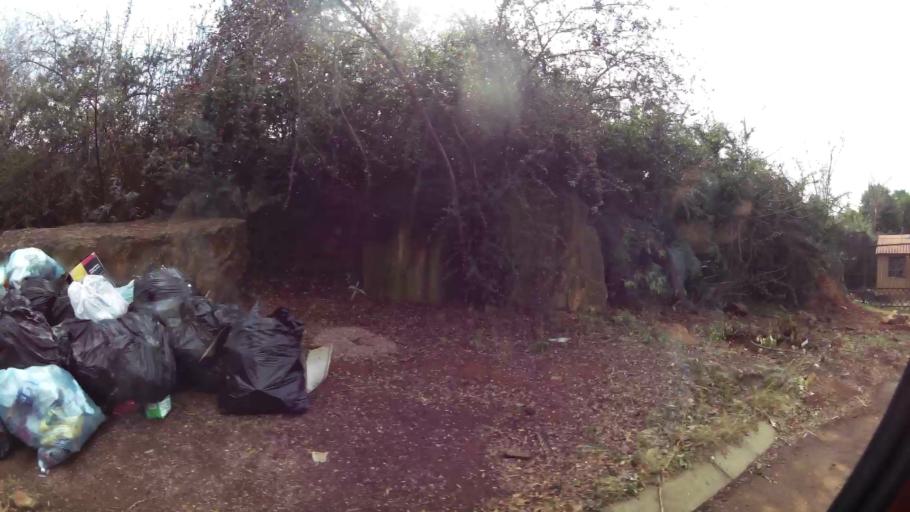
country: ZA
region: Gauteng
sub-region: Sedibeng District Municipality
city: Vanderbijlpark
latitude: -26.7480
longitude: 27.8378
